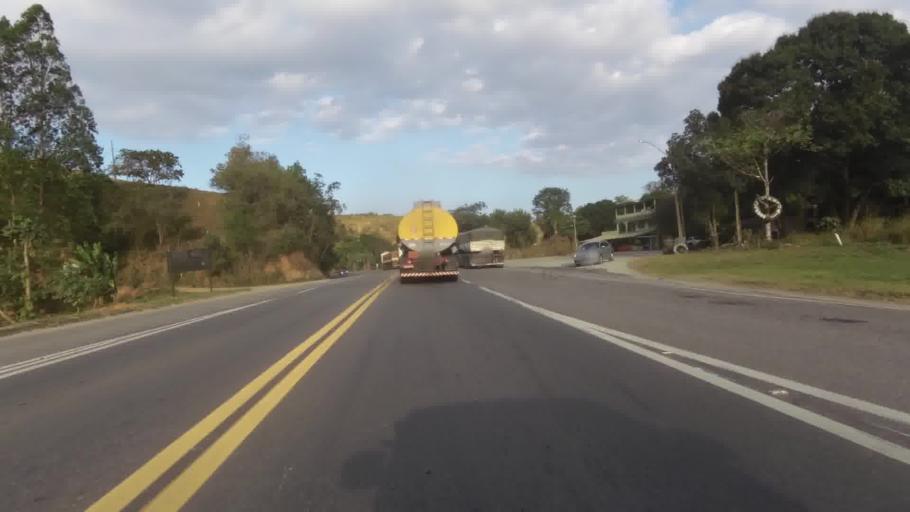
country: BR
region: Espirito Santo
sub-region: Rio Novo Do Sul
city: Rio Novo do Sul
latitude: -20.8897
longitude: -40.9939
